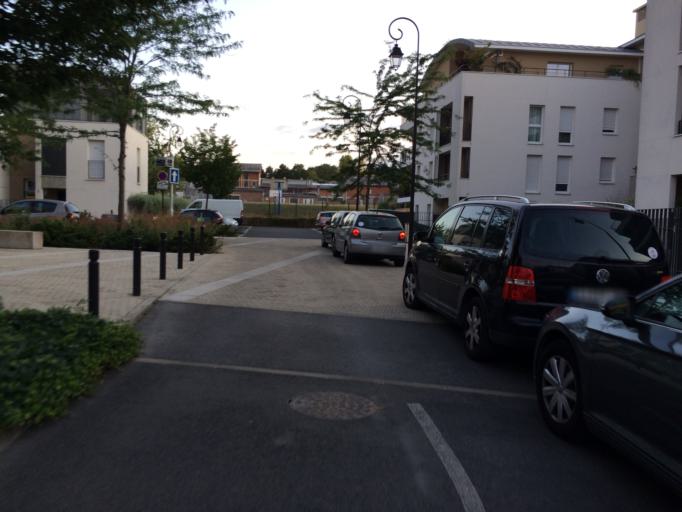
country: FR
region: Ile-de-France
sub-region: Departement du Val-de-Marne
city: Fresnes
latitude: 48.7490
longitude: 2.3190
